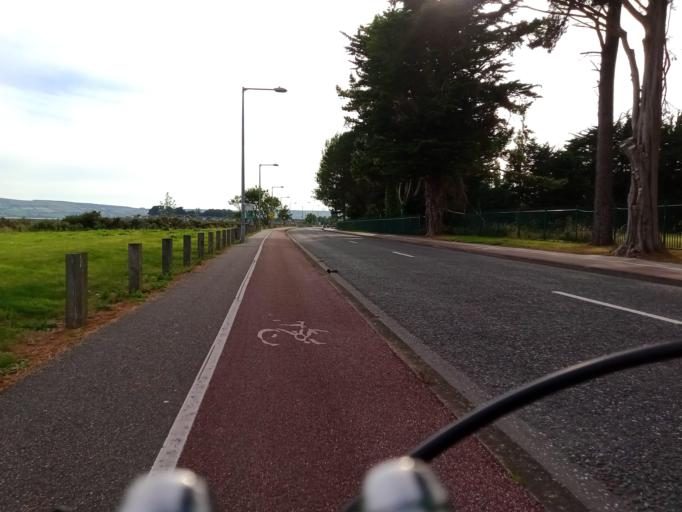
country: IE
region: Munster
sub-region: Waterford
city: Dungarvan
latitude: 52.1000
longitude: -7.5879
